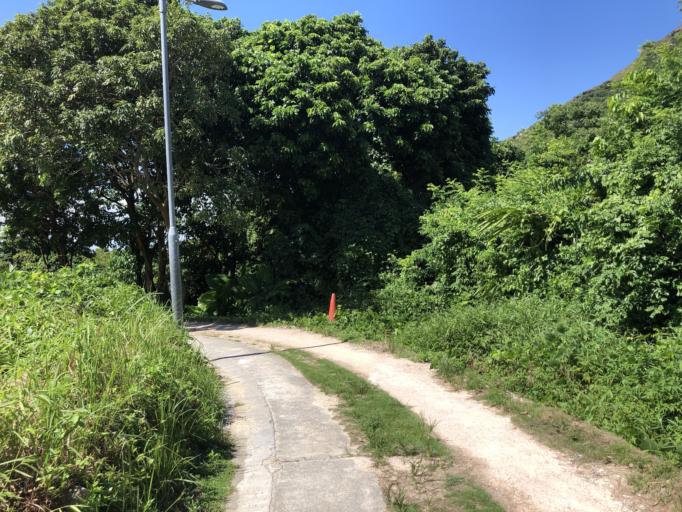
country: HK
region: Tuen Mun
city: Tuen Mun
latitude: 22.2901
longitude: 113.9789
